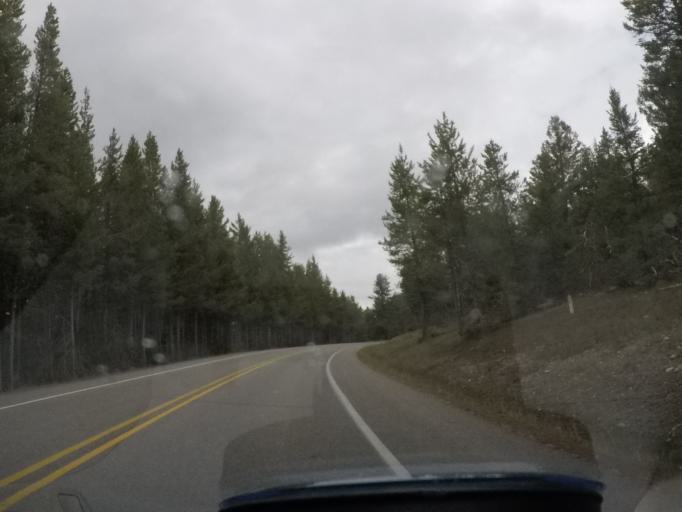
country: US
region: Wyoming
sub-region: Teton County
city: Moose Wilson Road
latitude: 43.9335
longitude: -110.6319
